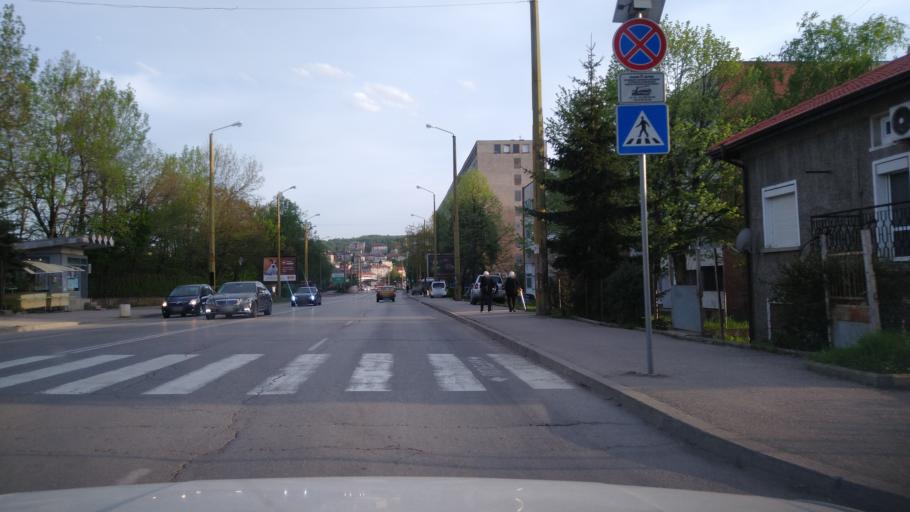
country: BG
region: Gabrovo
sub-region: Obshtina Gabrovo
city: Gabrovo
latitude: 42.8845
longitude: 25.3130
